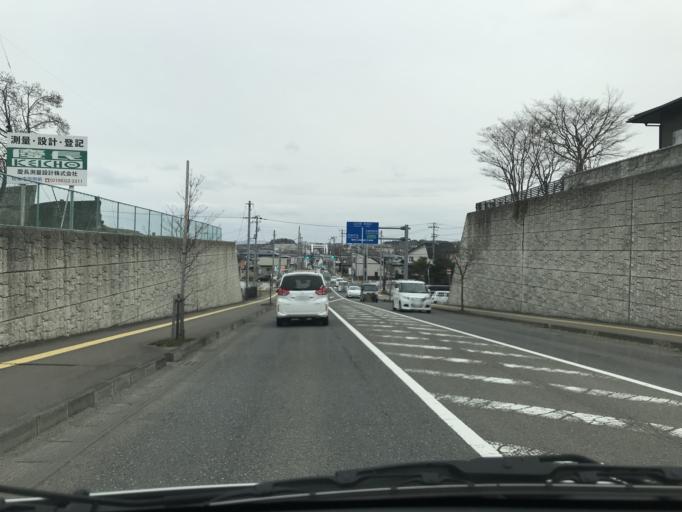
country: JP
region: Iwate
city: Hanamaki
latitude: 39.3852
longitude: 141.1097
